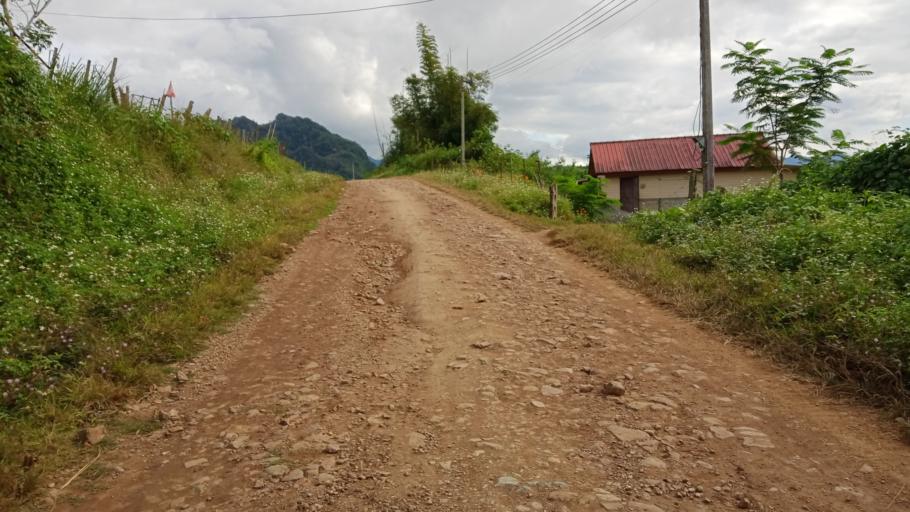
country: LA
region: Xiangkhoang
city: Phonsavan
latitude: 19.1063
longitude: 102.9295
